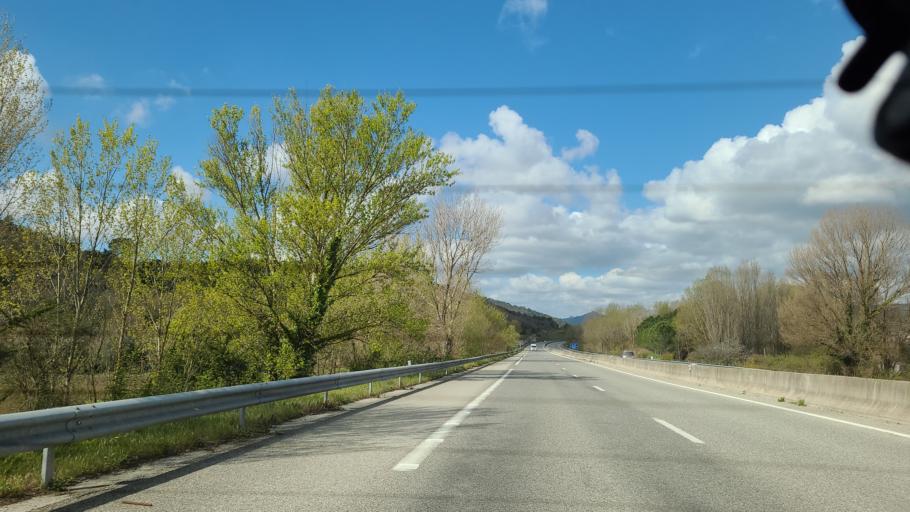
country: FR
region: Provence-Alpes-Cote d'Azur
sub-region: Departement du Var
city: Pignans
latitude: 43.2896
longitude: 6.2163
